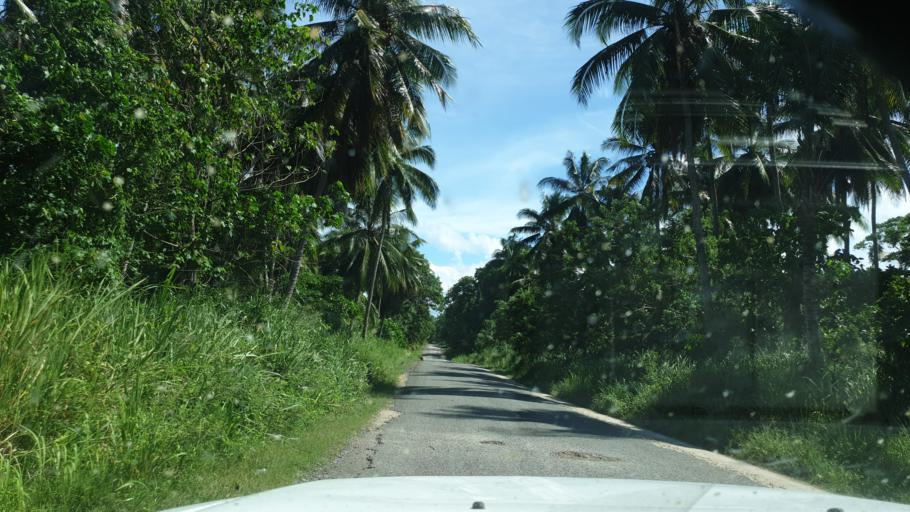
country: PG
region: Madang
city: Madang
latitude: -4.6636
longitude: 145.5819
